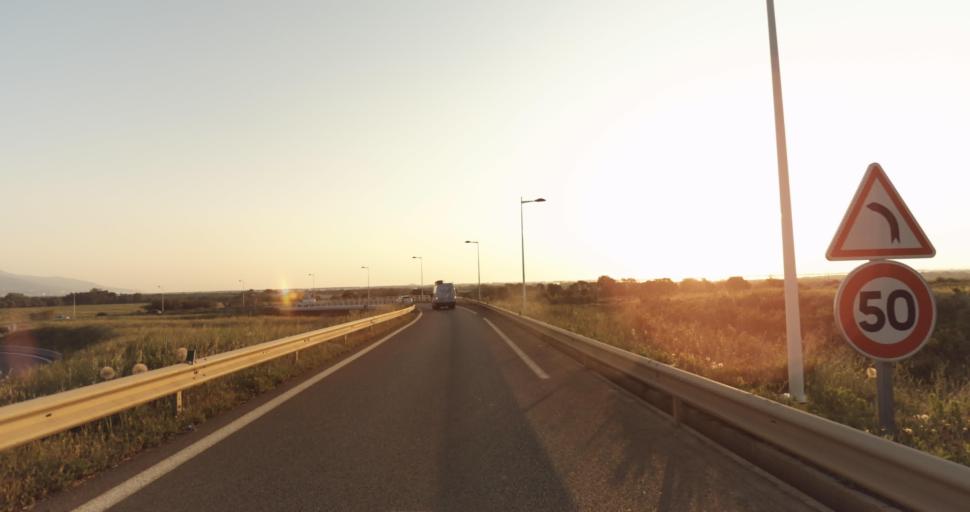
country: FR
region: Corsica
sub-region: Departement de la Haute-Corse
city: Borgo
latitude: 42.5697
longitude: 9.4416
